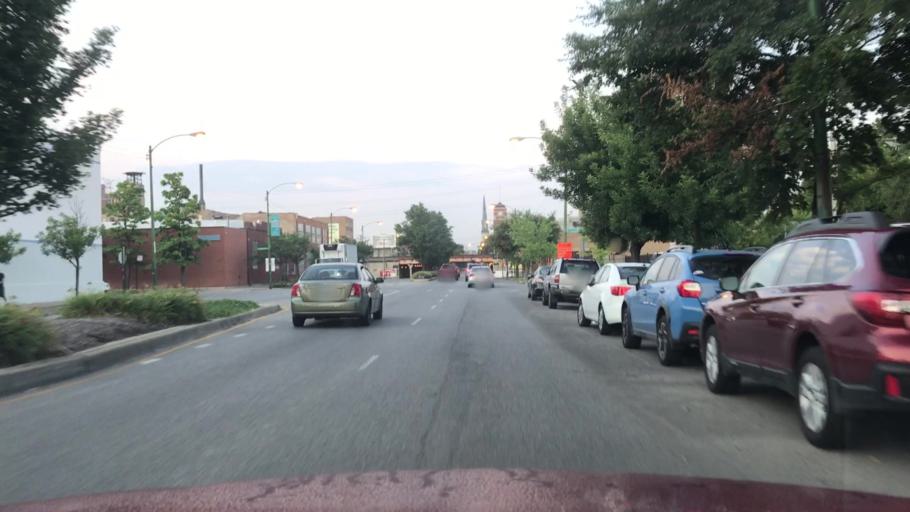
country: US
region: Illinois
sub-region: Cook County
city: Chicago
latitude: 41.8905
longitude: -87.6672
